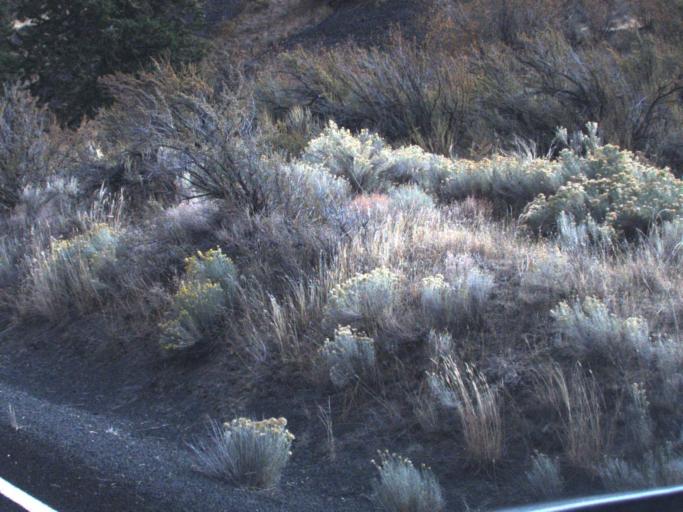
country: US
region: Washington
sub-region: Okanogan County
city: Coulee Dam
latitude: 47.9002
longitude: -118.7015
